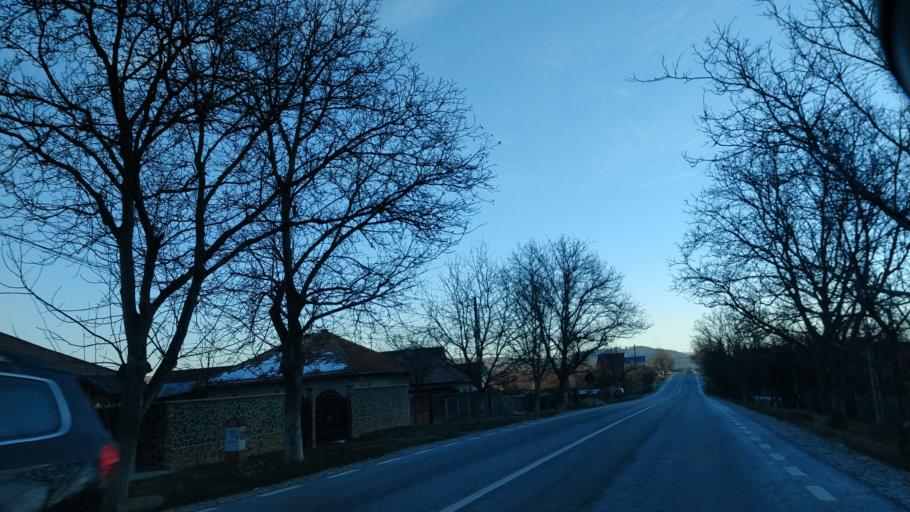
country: RO
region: Bacau
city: Gura Vaii
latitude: 46.3186
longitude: 26.7485
